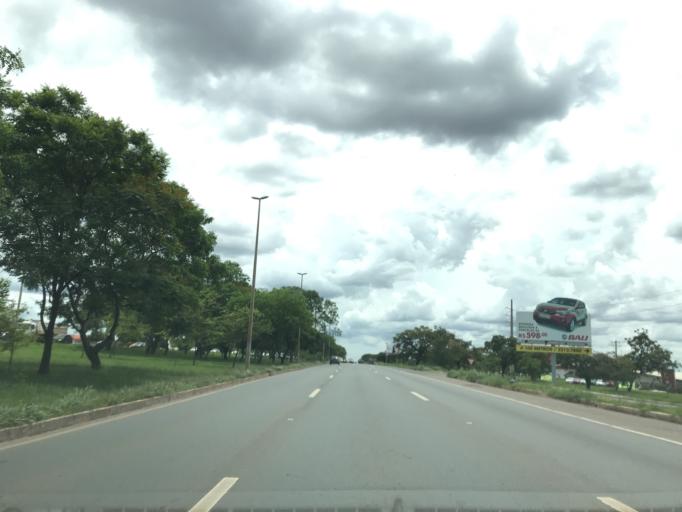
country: BR
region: Federal District
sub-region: Brasilia
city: Brasilia
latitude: -15.7625
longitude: -47.9312
